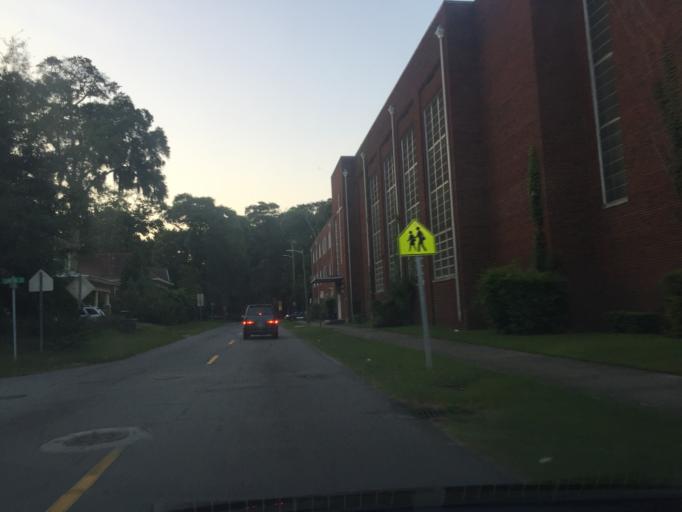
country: US
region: Georgia
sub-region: Chatham County
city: Thunderbolt
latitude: 32.0593
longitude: -81.0667
